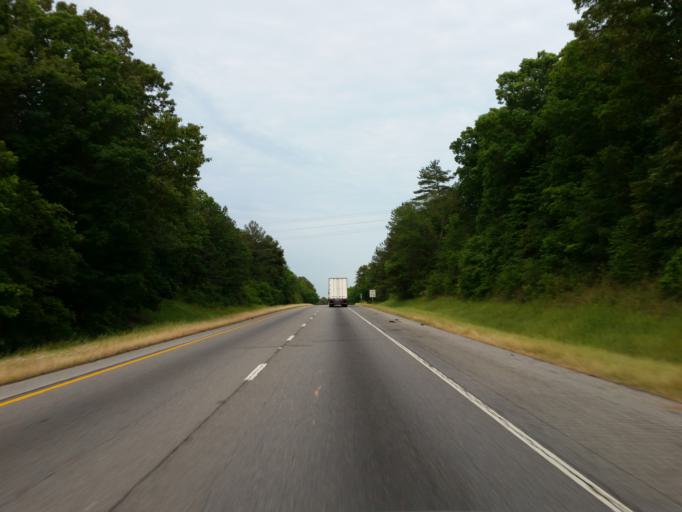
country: US
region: Alabama
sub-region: Talladega County
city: Lincoln
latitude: 33.5895
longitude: -86.1103
